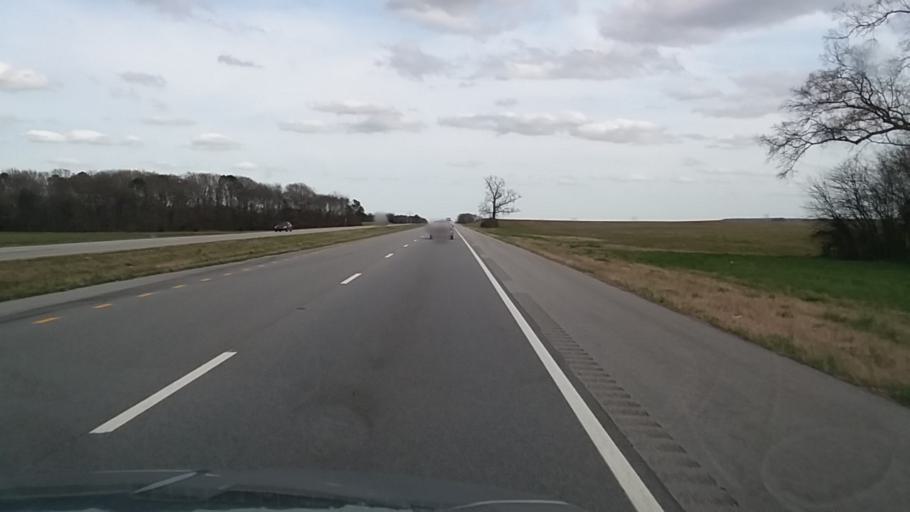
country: US
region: Alabama
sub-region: Lawrence County
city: Town Creek
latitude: 34.6827
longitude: -87.4803
